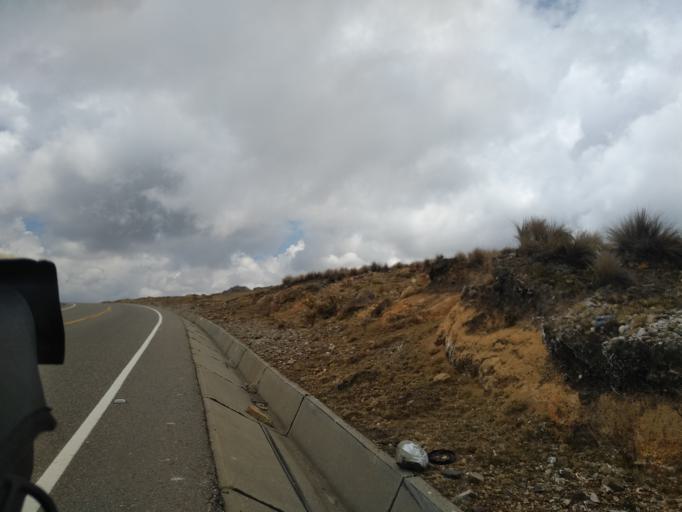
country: PE
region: La Libertad
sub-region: Provincia de Santiago de Chuco
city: Quiruvilca
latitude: -7.9650
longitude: -78.1984
